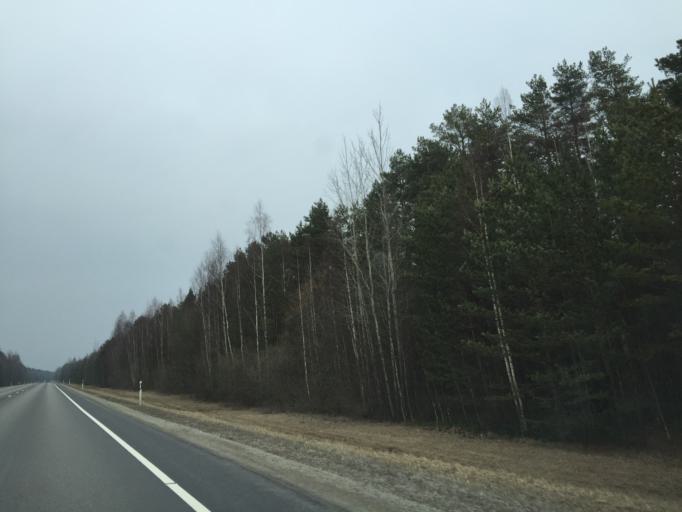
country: LV
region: Salacgrivas
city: Ainazi
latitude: 58.0936
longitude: 24.5079
